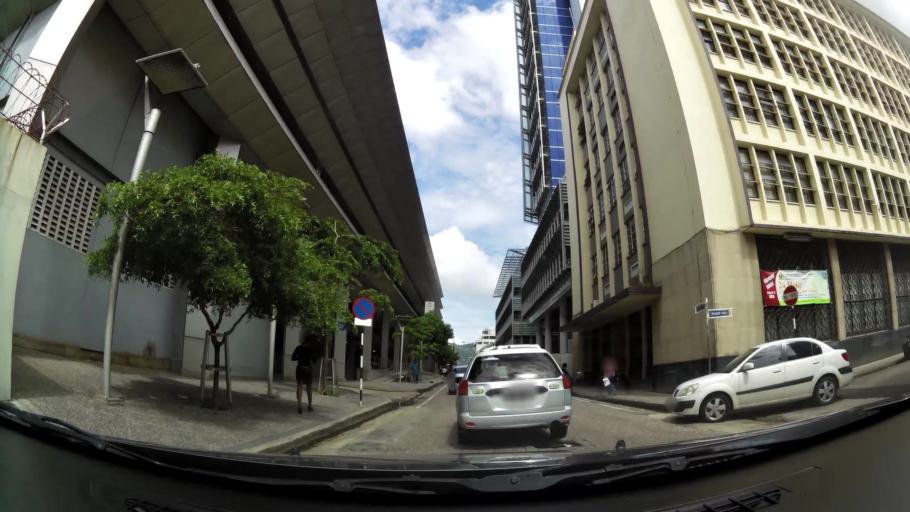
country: TT
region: San Juan/Laventille
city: Laventille
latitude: 10.6501
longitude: -61.5129
